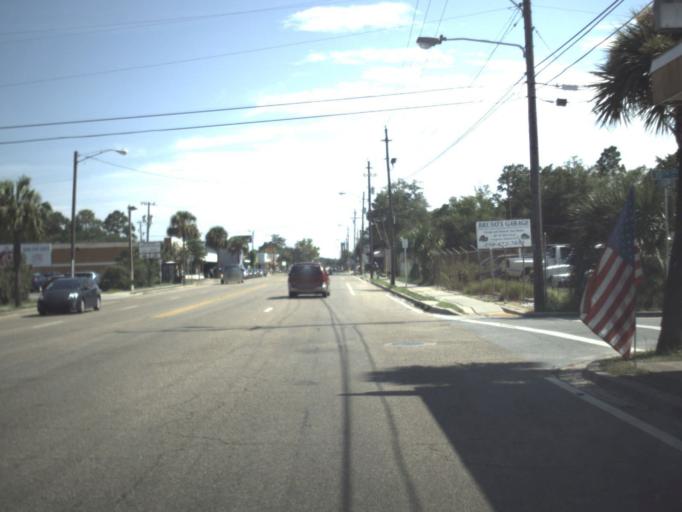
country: US
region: Florida
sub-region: Bay County
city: Panama City
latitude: 30.1662
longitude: -85.6603
